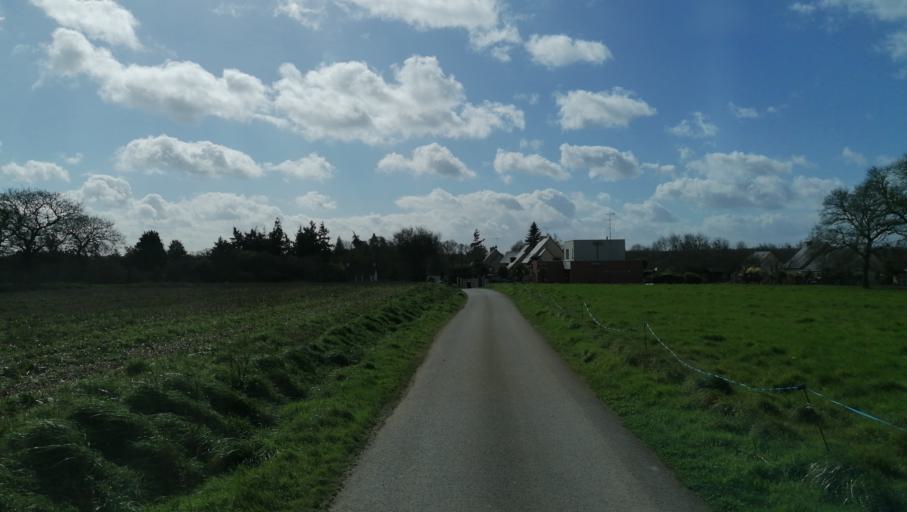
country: FR
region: Brittany
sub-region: Departement des Cotes-d'Armor
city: Pleguien
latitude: 48.6369
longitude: -2.9288
